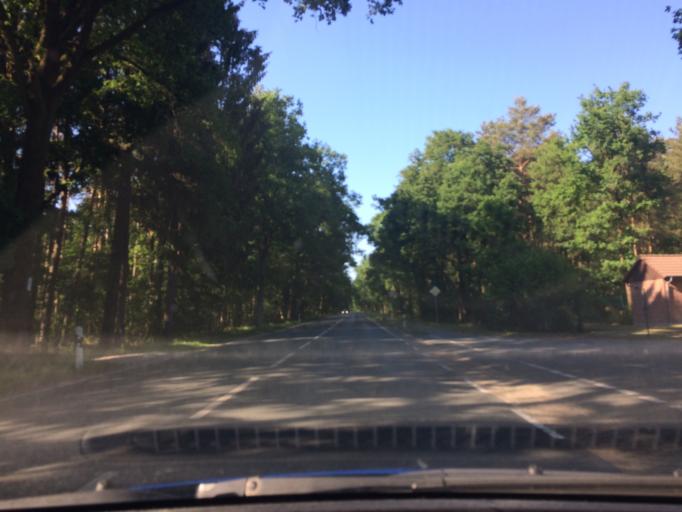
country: DE
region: Lower Saxony
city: Soltau
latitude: 53.0123
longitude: 9.8447
